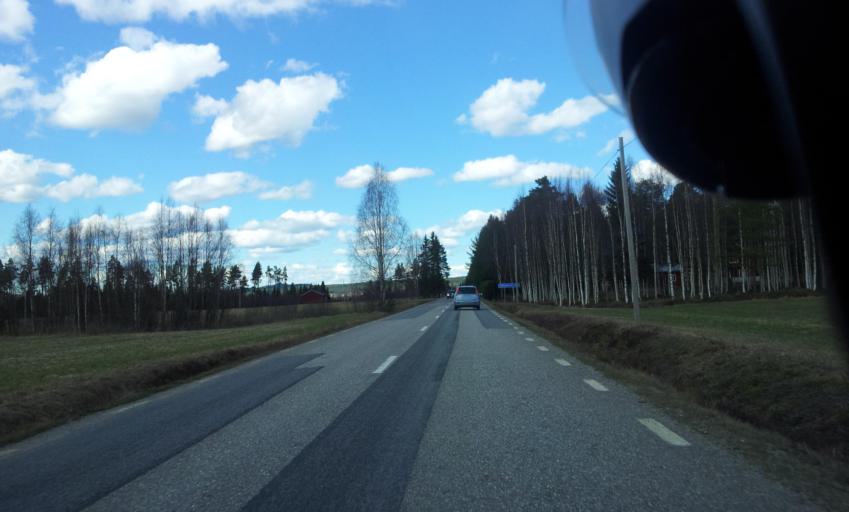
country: SE
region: Gaevleborg
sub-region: Ovanakers Kommun
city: Edsbyn
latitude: 61.3003
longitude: 15.8899
